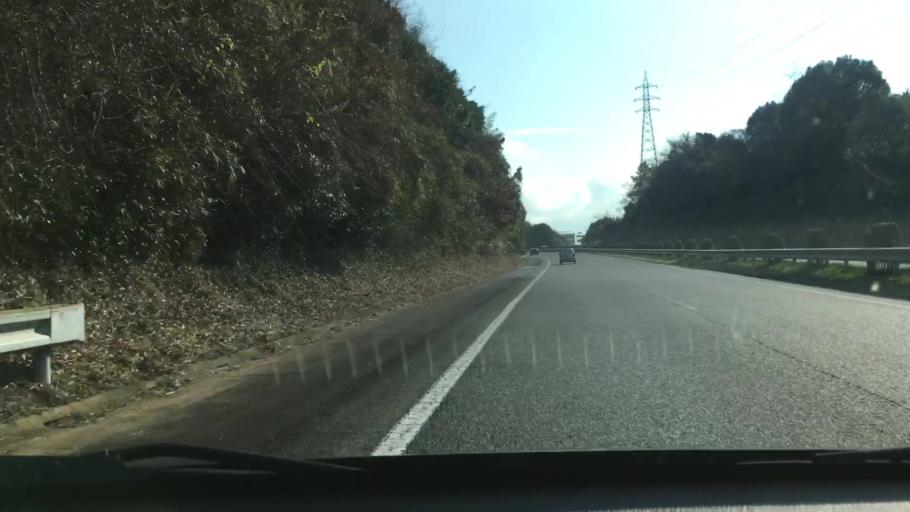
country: JP
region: Kumamoto
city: Matsubase
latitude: 32.6335
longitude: 130.7102
